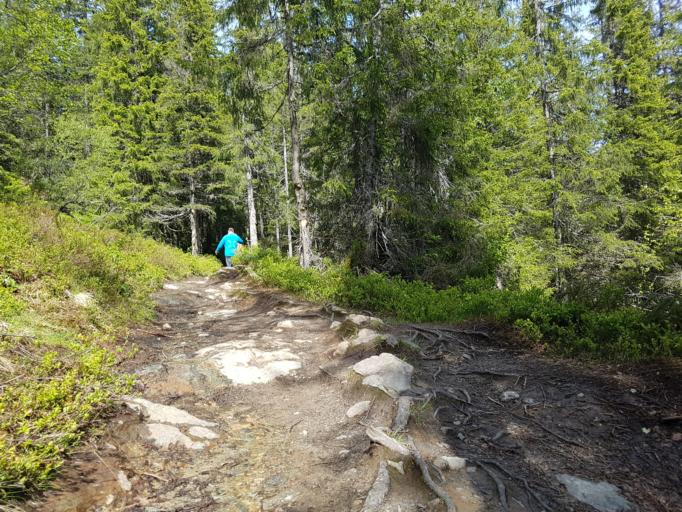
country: NO
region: Sor-Trondelag
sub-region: Trondheim
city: Trondheim
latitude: 63.4276
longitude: 10.3052
